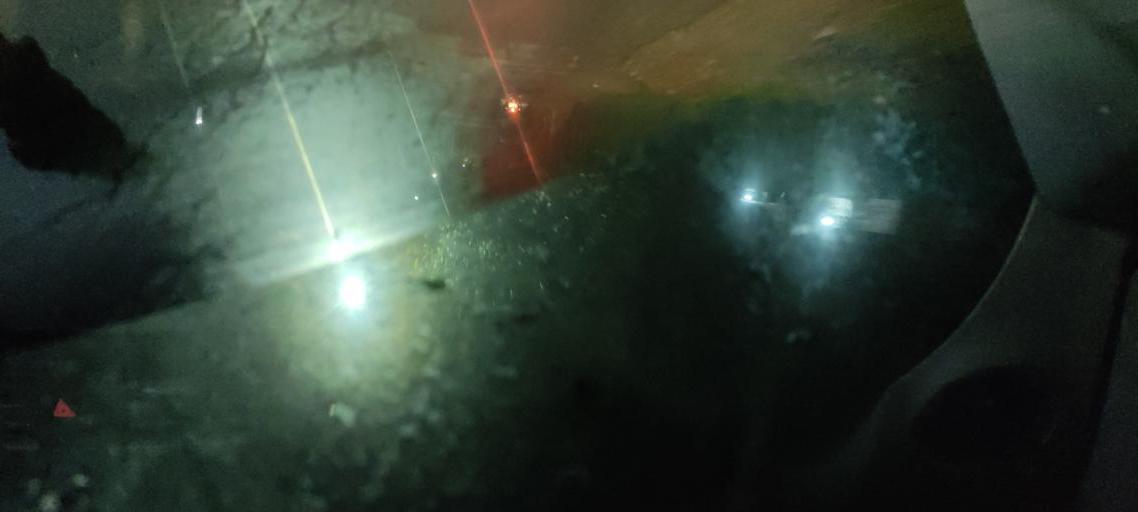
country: IN
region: Kerala
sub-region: Alappuzha
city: Vayalar
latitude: 9.7234
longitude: 76.3342
